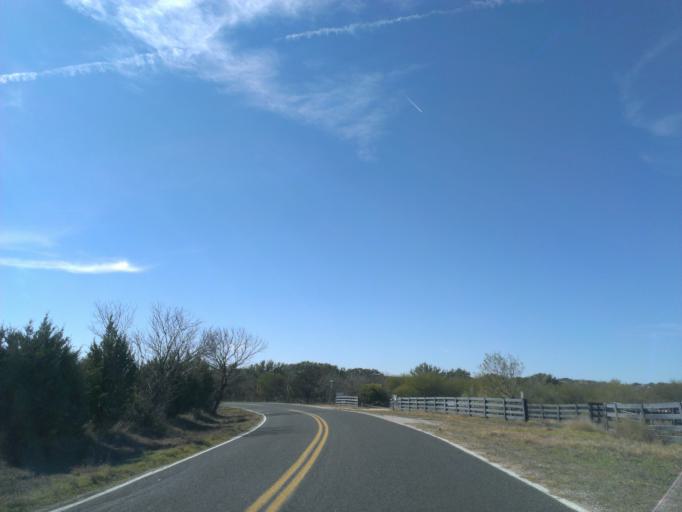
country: US
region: Texas
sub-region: Travis County
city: Briarcliff
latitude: 30.4545
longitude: -98.0838
